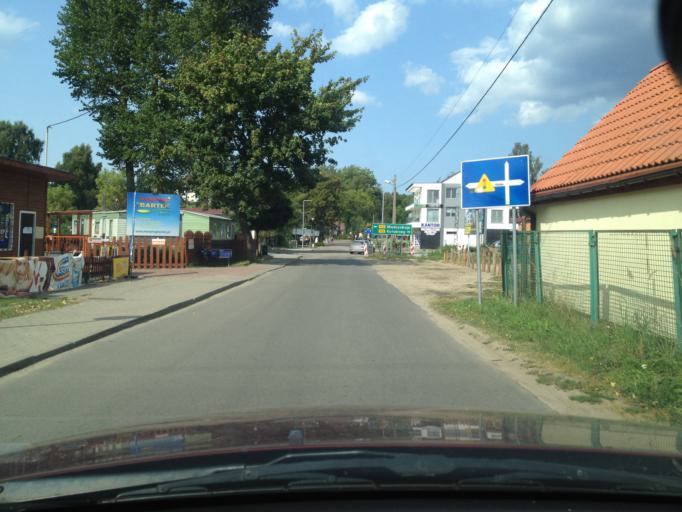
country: PL
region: West Pomeranian Voivodeship
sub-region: Powiat gryficki
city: Pobierowo
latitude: 54.0422
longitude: 14.8736
